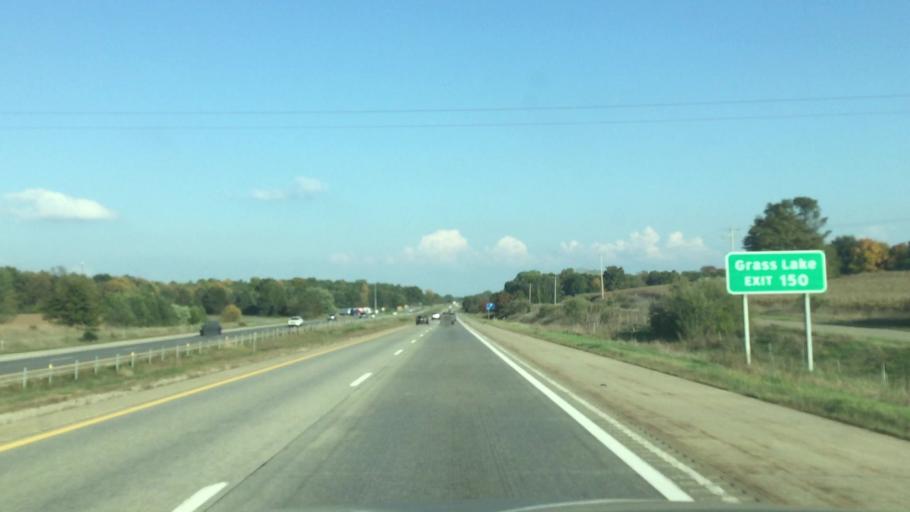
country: US
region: Michigan
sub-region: Jackson County
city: Grass Lake
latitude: 42.2918
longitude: -84.2229
